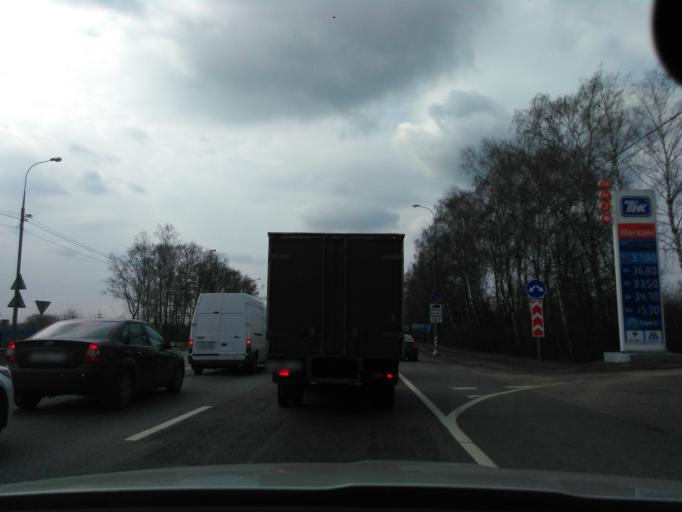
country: RU
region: Moskovskaya
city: Sheremet'yevskiy
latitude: 55.9962
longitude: 37.5351
